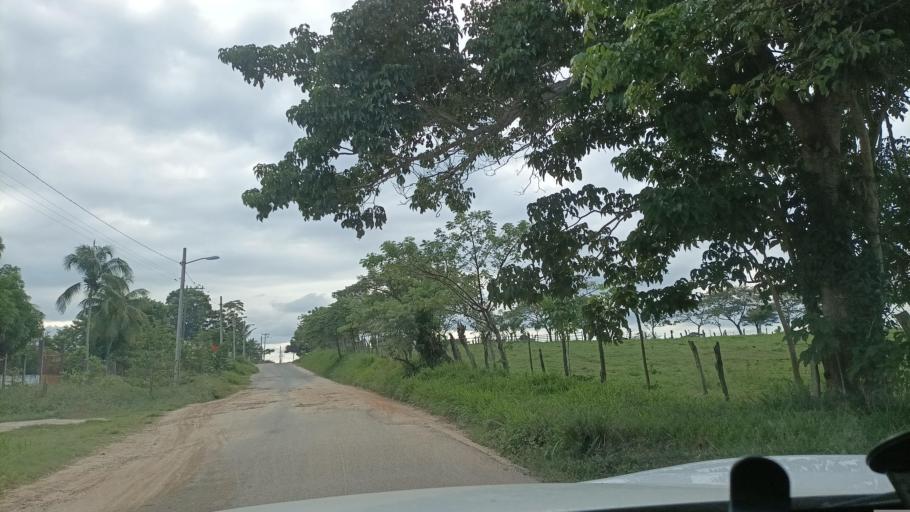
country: MX
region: Veracruz
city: Oluta
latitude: 17.9264
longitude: -94.8850
